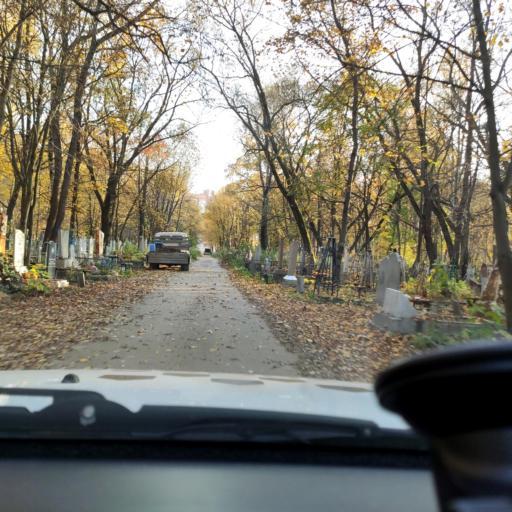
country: RU
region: Perm
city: Perm
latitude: 57.9902
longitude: 56.2815
